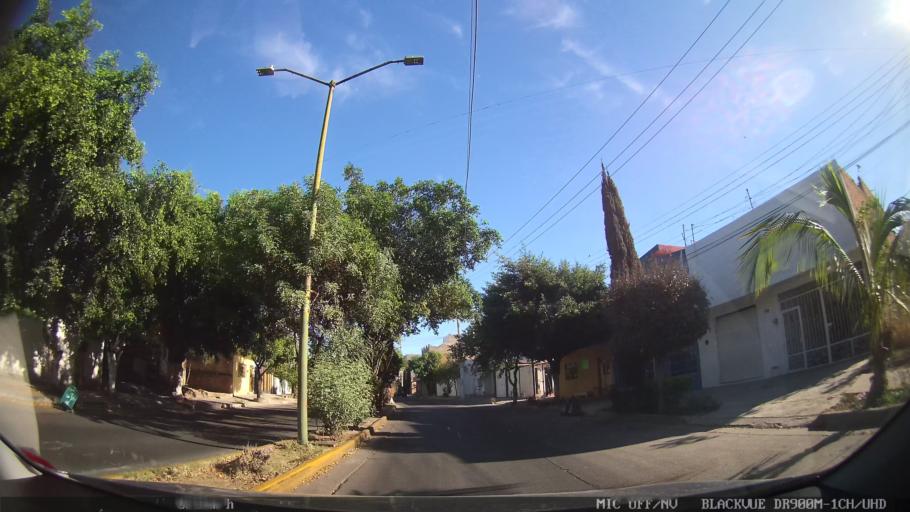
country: MX
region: Jalisco
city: Tlaquepaque
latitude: 20.6828
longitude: -103.2777
